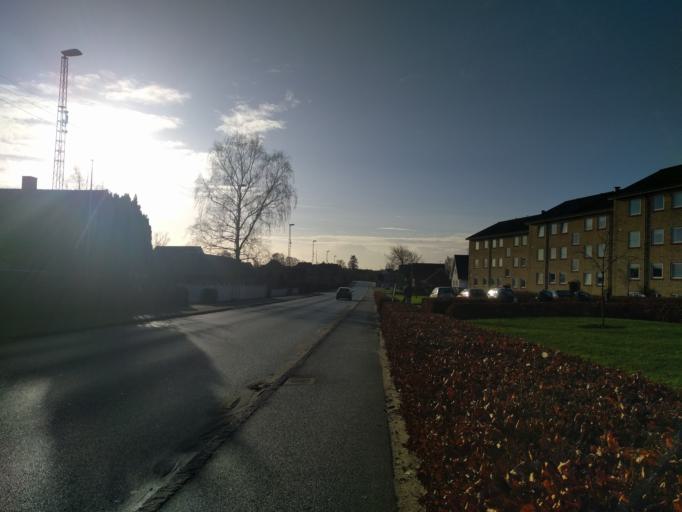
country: DK
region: Central Jutland
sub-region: Viborg Kommune
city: Viborg
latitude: 56.4630
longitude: 9.4165
